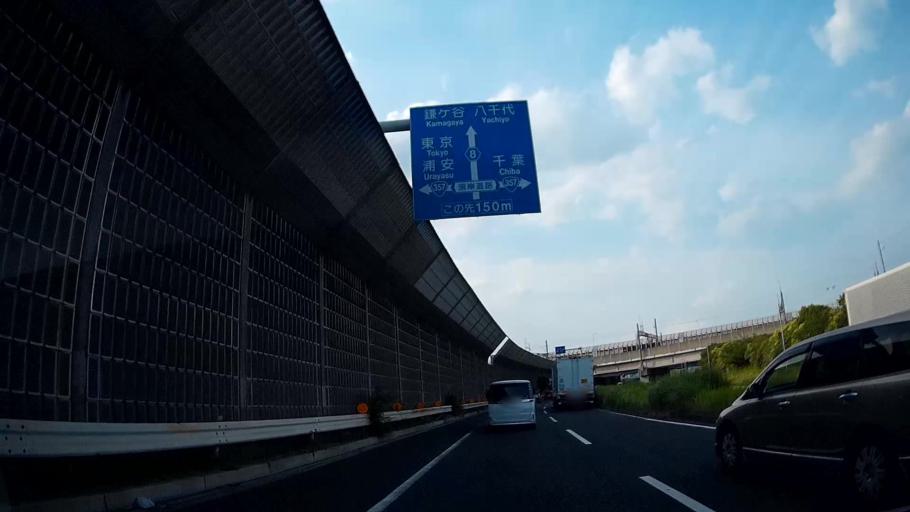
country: JP
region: Chiba
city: Funabashi
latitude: 35.6792
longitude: 139.9982
